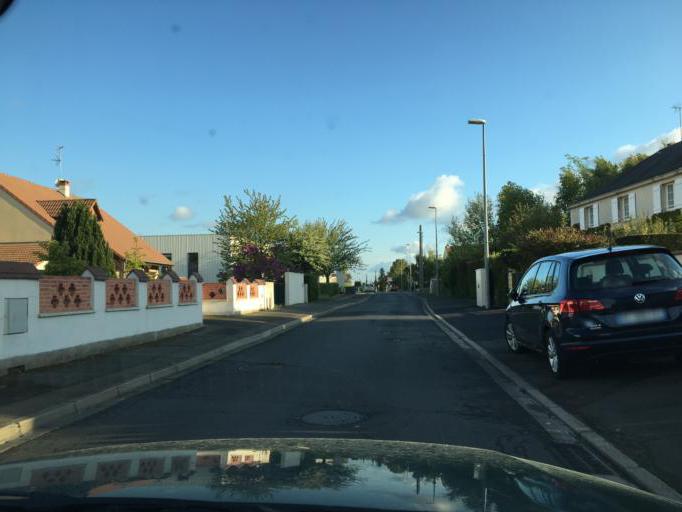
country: FR
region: Centre
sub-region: Departement du Loiret
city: Semoy
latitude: 47.9256
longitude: 1.9377
